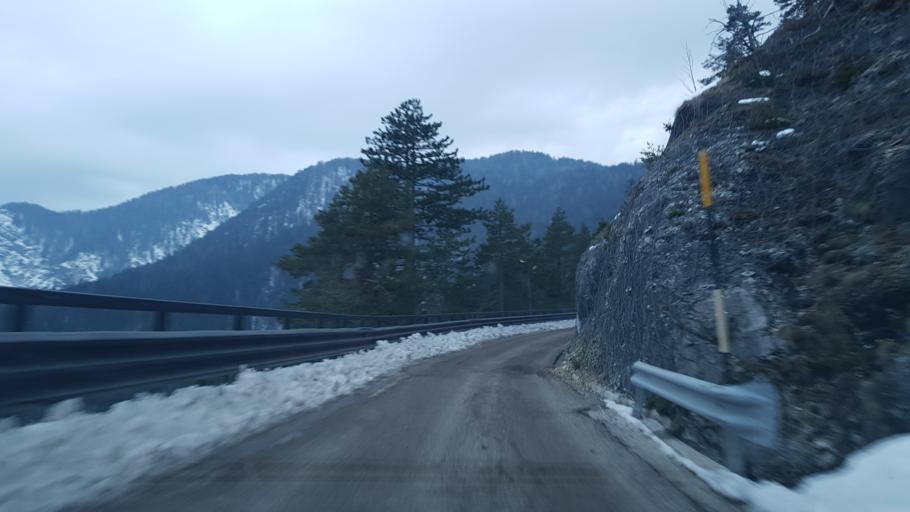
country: IT
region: Friuli Venezia Giulia
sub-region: Provincia di Udine
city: Malborghetto
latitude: 46.5163
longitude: 13.4735
